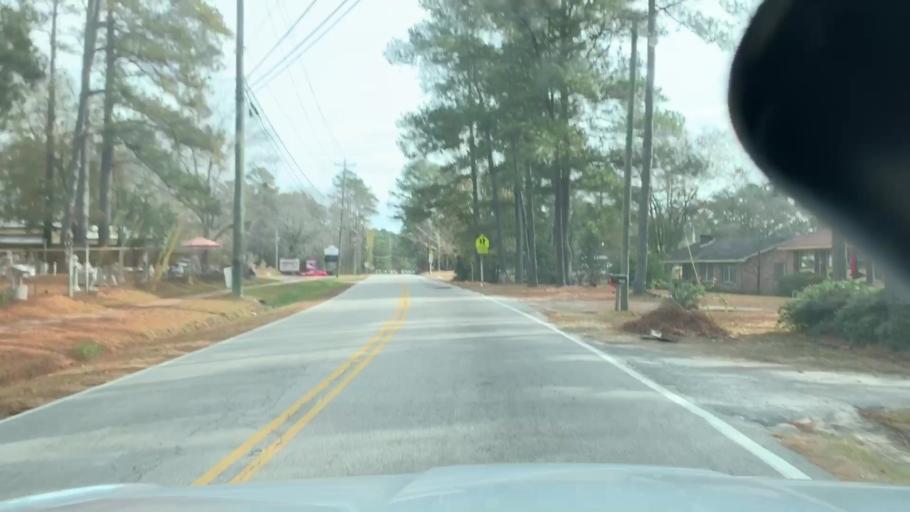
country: US
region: South Carolina
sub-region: Richland County
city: Woodfield
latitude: 34.0817
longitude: -80.9293
